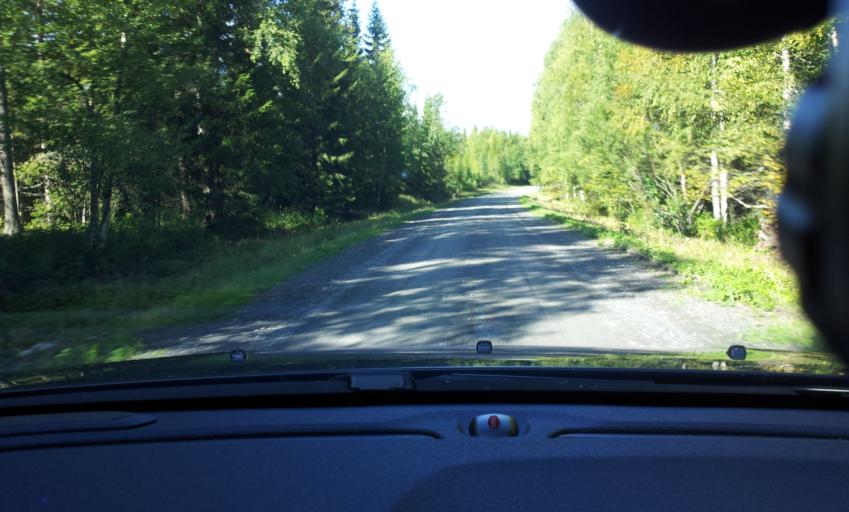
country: SE
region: Jaemtland
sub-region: Krokoms Kommun
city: Valla
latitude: 63.2684
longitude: 13.7683
